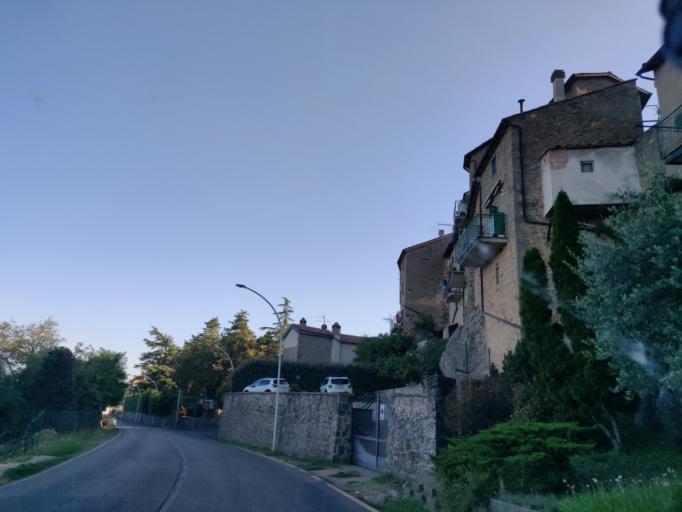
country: IT
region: Tuscany
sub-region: Provincia di Siena
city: Piancastagnaio
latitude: 42.8492
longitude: 11.6951
